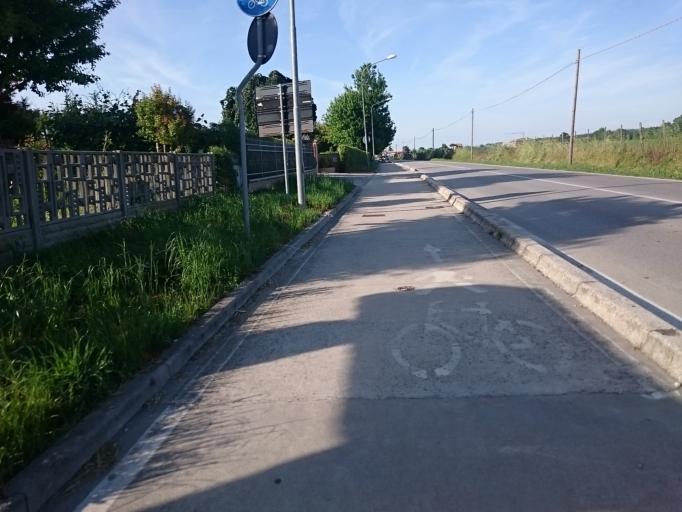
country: IT
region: Veneto
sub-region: Provincia di Padova
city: Terradura
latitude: 45.3510
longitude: 11.8189
